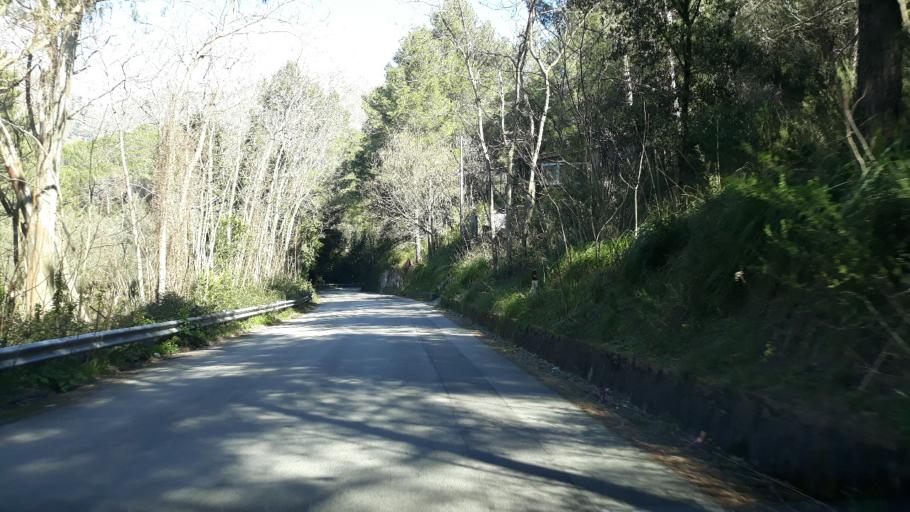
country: IT
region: Sicily
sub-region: Palermo
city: Piano dei Geli
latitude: 38.0909
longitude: 13.2590
